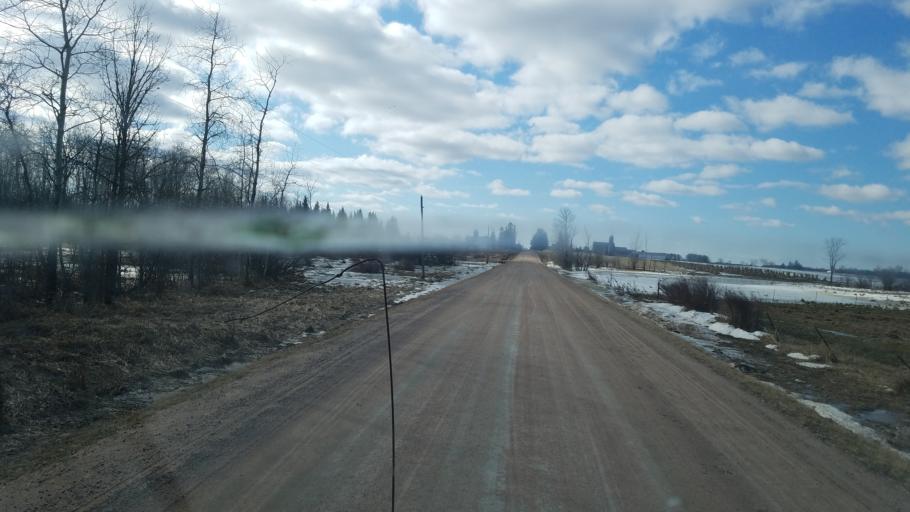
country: US
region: Wisconsin
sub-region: Clark County
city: Loyal
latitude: 44.6535
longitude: -90.3978
